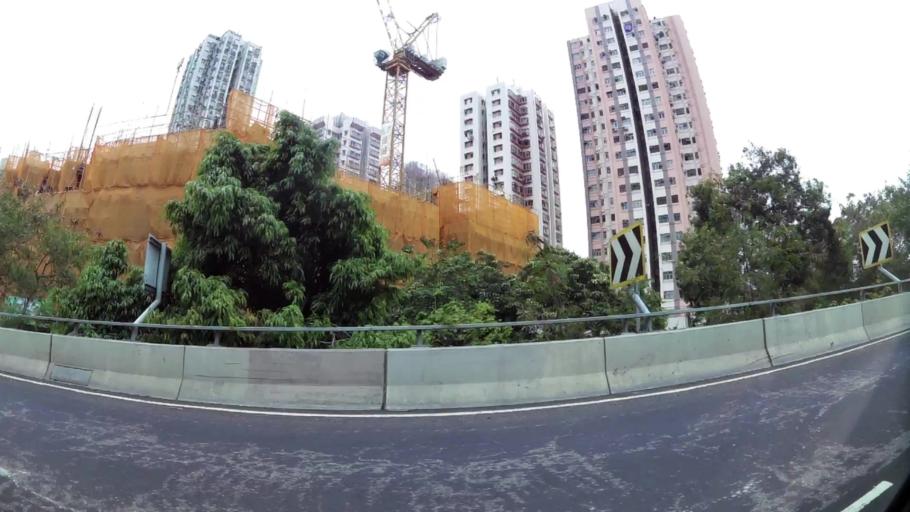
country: HK
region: Tuen Mun
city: Tuen Mun
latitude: 22.4045
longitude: 113.9782
